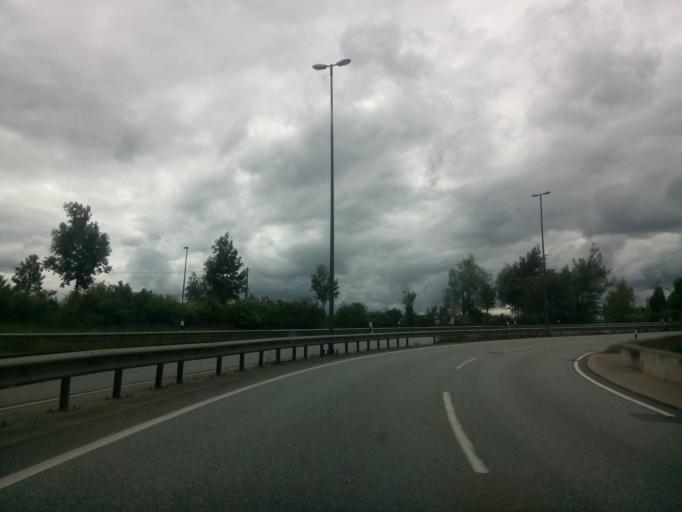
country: DE
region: Bremen
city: Bremen
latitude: 53.0679
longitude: 8.7743
